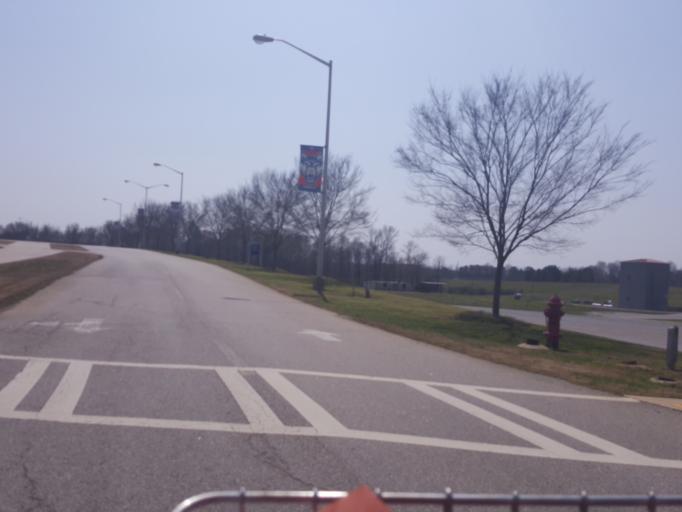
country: US
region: Georgia
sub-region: Carroll County
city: Carrollton
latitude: 33.5812
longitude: -85.1217
